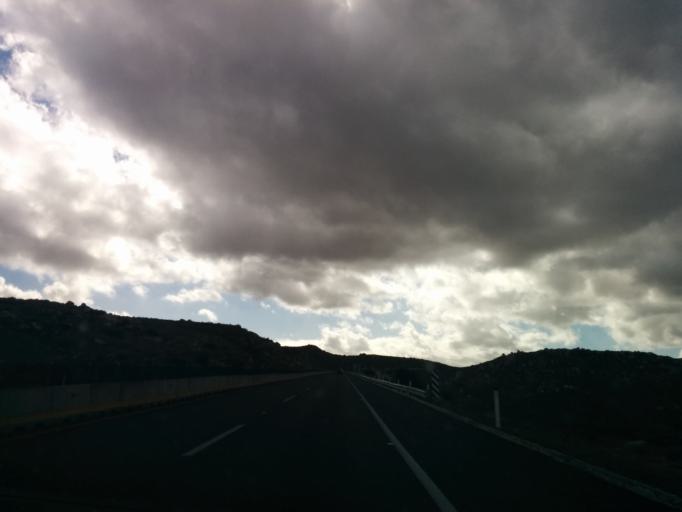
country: MX
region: Baja California
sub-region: Tijuana
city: Villa del Campo
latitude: 32.5332
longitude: -116.7401
